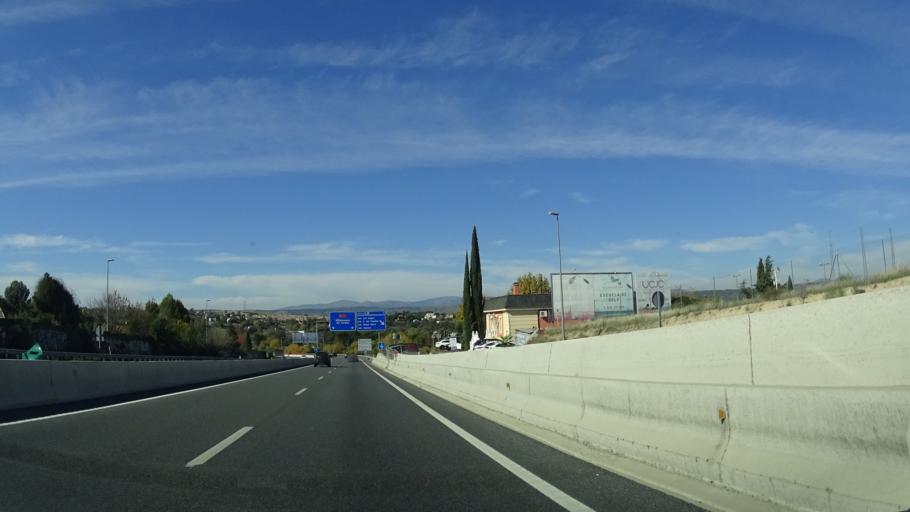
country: ES
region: Madrid
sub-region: Provincia de Madrid
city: Villanueva del Pardillo
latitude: 40.4843
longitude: -3.9326
